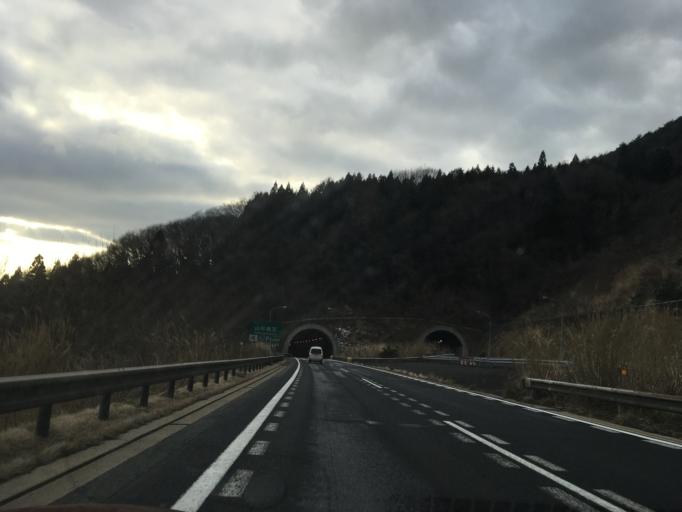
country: JP
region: Yamagata
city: Yamagata-shi
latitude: 38.2437
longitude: 140.4020
